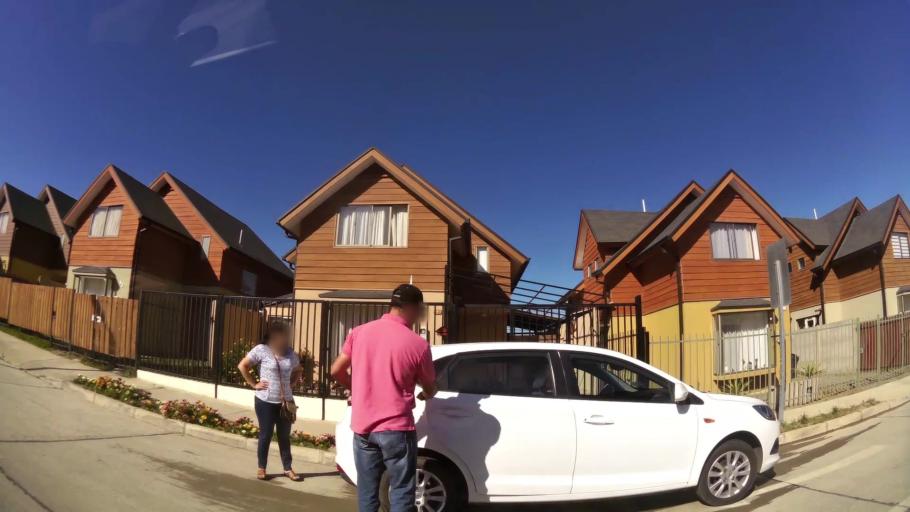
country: CL
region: Valparaiso
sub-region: Provincia de Valparaiso
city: Vina del Mar
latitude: -33.1277
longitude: -71.5705
